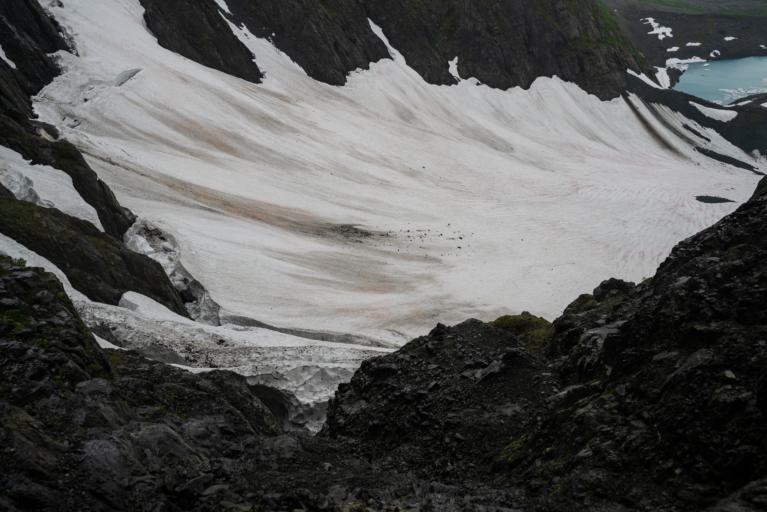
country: RU
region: Komi Republic
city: Synya
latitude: 64.7801
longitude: 58.8822
